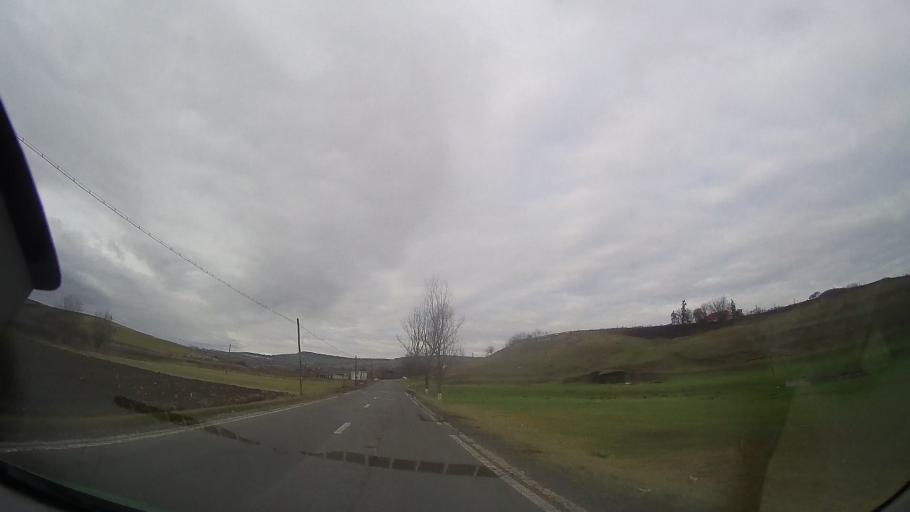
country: RO
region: Bistrita-Nasaud
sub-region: Comuna Urmenis
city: Urmenis
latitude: 46.7644
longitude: 24.3749
